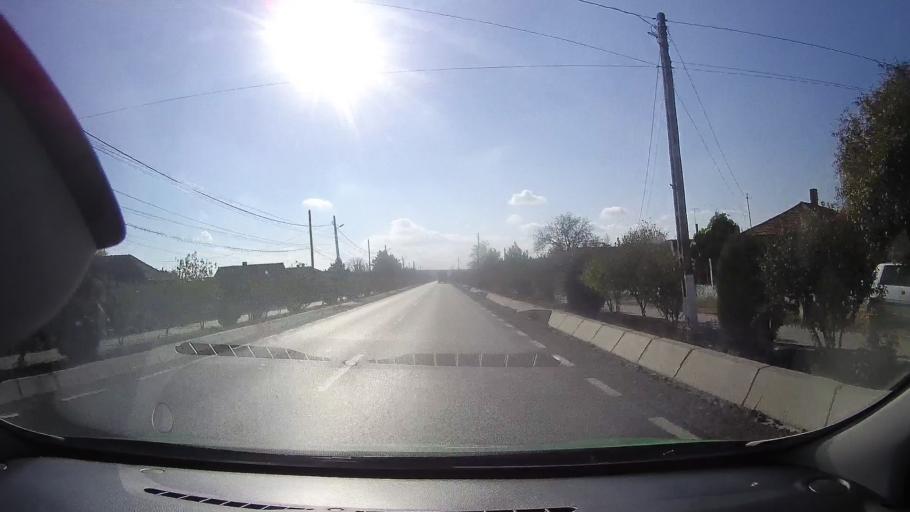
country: RO
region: Tulcea
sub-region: Comuna Baia
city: Baia
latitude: 44.7309
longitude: 28.6816
